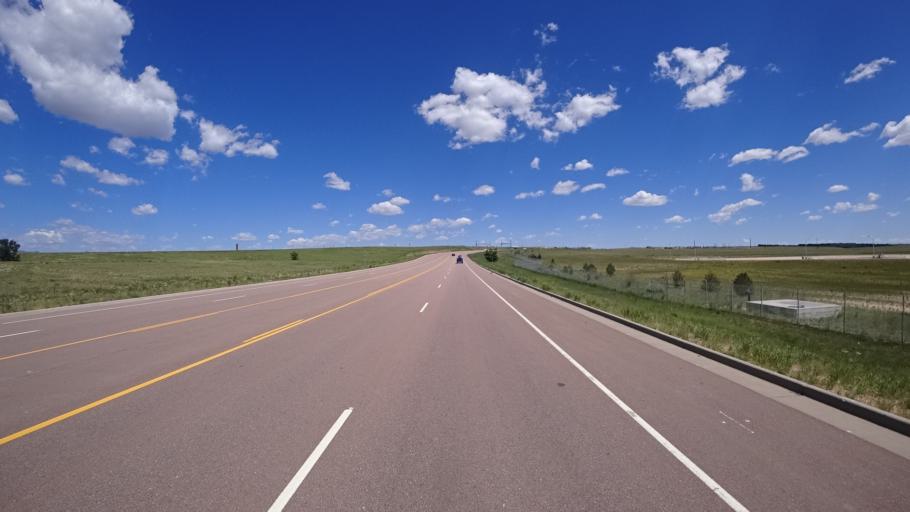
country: US
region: Colorado
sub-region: El Paso County
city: Cimarron Hills
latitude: 38.8465
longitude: -104.6827
